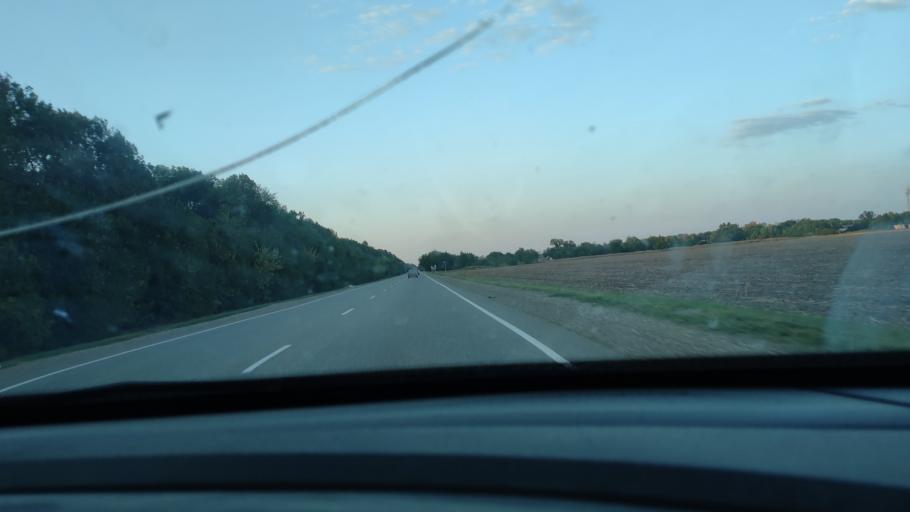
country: RU
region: Krasnodarskiy
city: Novominskaya
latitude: 46.4058
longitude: 39.0005
